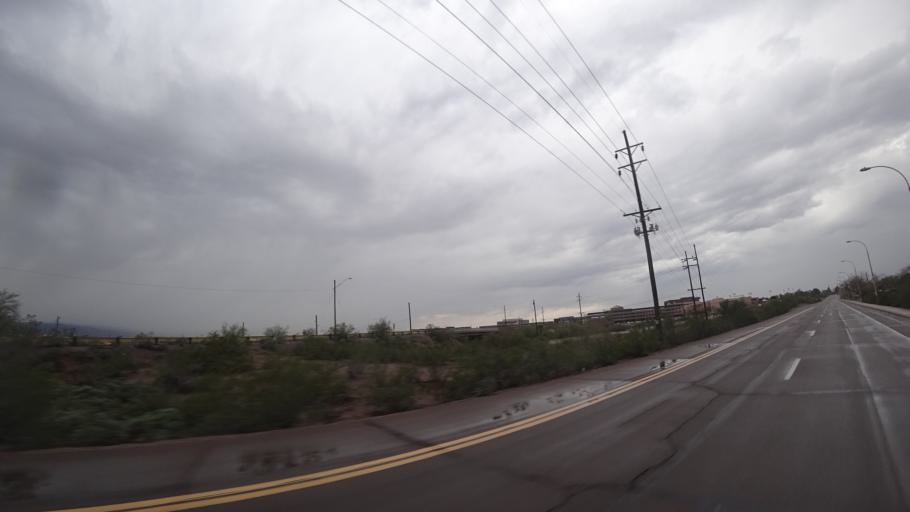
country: US
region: Arizona
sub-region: Maricopa County
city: Tempe Junction
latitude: 33.4431
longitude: -111.9473
